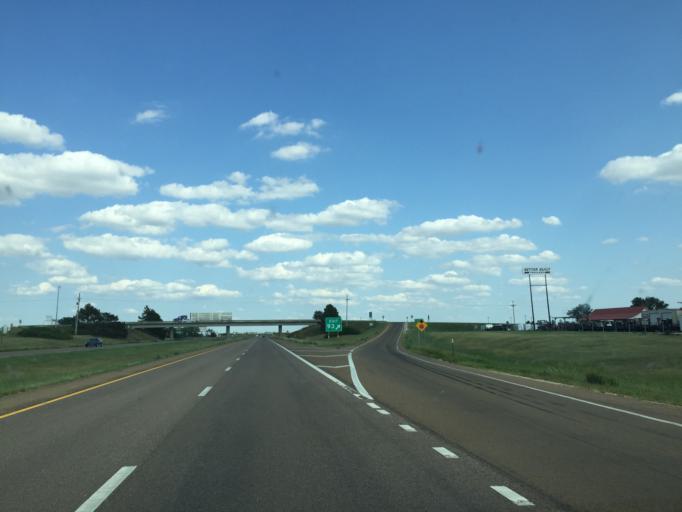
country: US
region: Kansas
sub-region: Gove County
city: Gove
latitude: 39.1100
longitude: -100.4821
